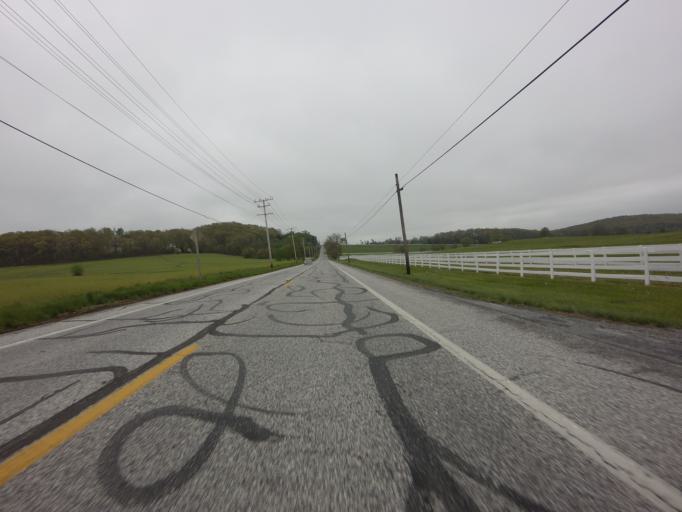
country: US
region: Maryland
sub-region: Baltimore County
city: Hunt Valley
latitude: 39.5774
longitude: -76.6611
